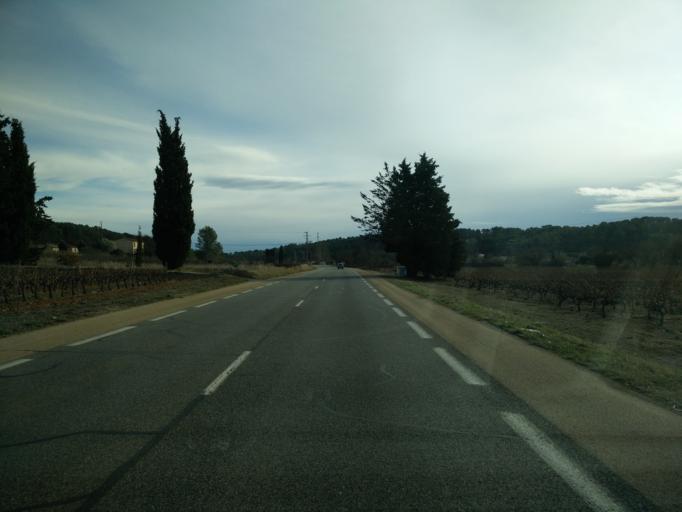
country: FR
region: Provence-Alpes-Cote d'Azur
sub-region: Departement du Var
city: Lorgues
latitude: 43.4807
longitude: 6.3711
